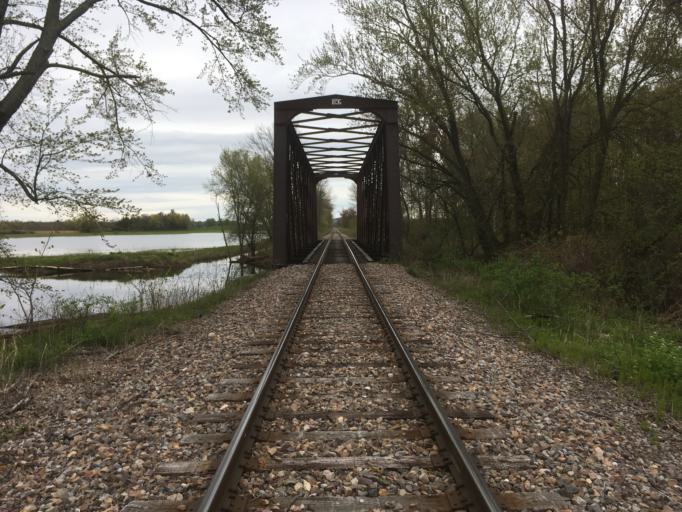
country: US
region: Vermont
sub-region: Addison County
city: Middlebury (village)
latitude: 43.9549
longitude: -73.1621
